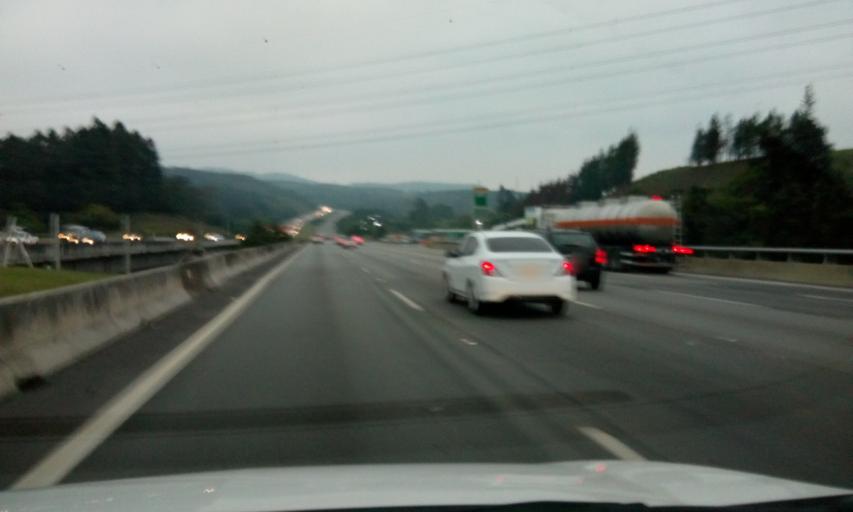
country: BR
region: Sao Paulo
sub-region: Caieiras
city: Caieiras
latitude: -23.3983
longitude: -46.7680
